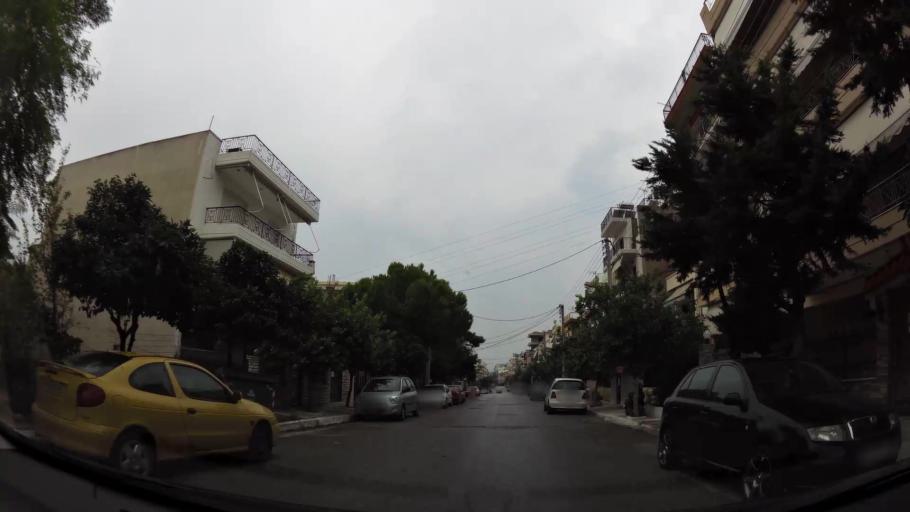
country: GR
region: Attica
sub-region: Nomos Piraios
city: Korydallos
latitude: 37.9927
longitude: 23.6510
